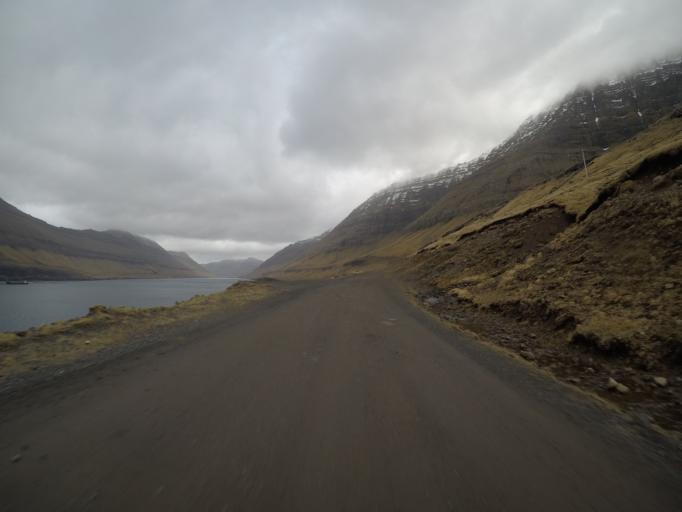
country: FO
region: Nordoyar
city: Klaksvik
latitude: 62.3456
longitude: -6.5798
